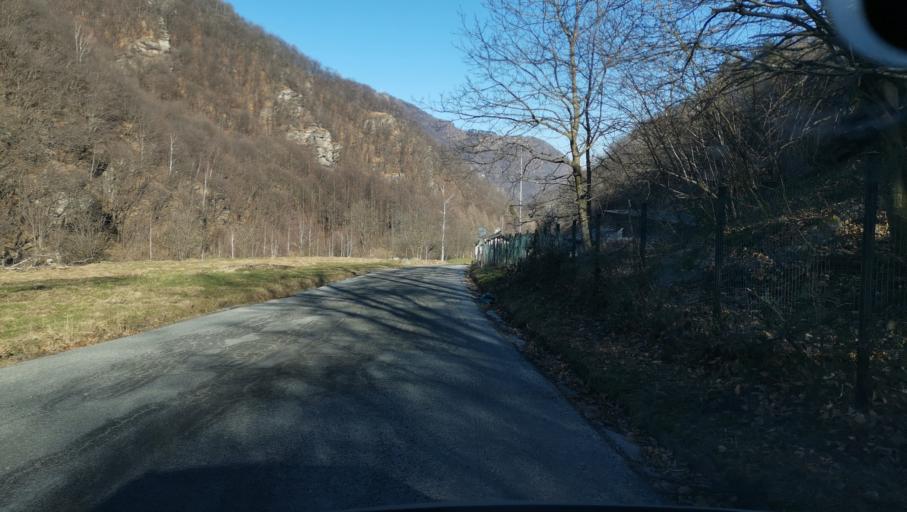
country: IT
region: Piedmont
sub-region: Provincia di Torino
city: Rora
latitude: 44.7728
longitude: 7.2051
